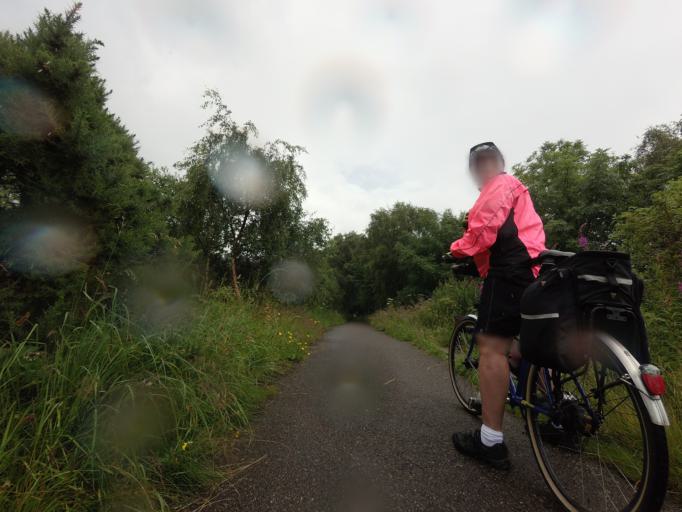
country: GB
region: Scotland
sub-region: Moray
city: Fochabers
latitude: 57.6627
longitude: -3.0954
